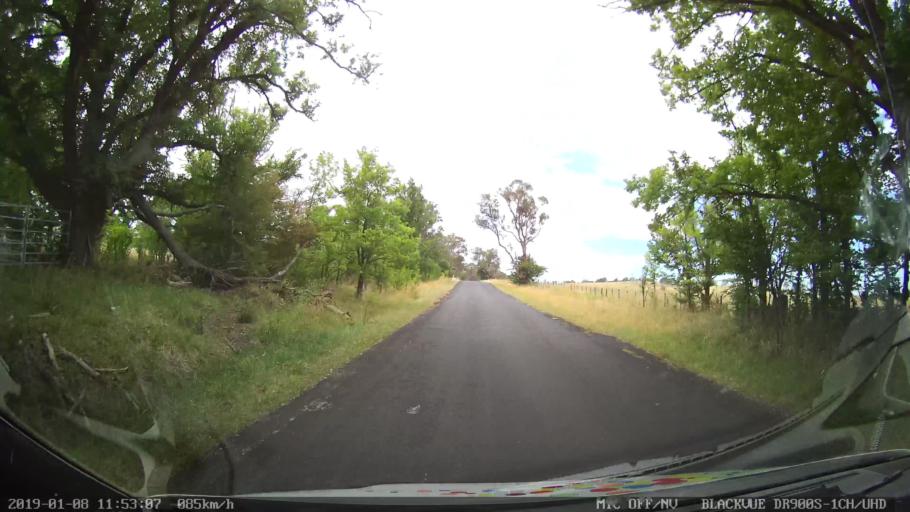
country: AU
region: New South Wales
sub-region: Armidale Dumaresq
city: Armidale
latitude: -30.4110
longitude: 151.5598
